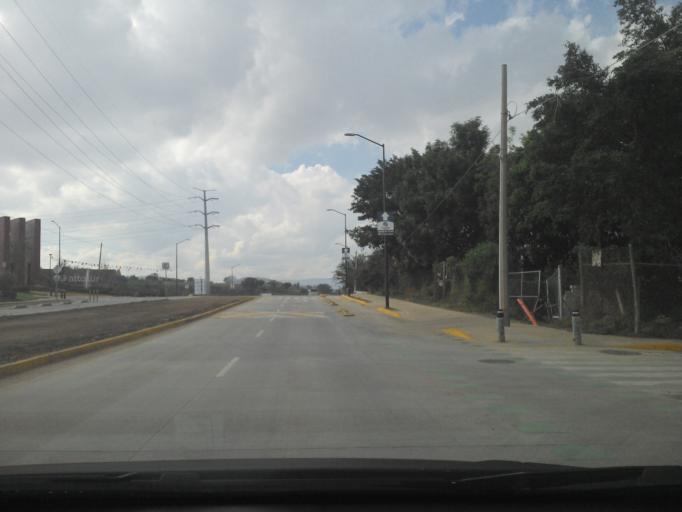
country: MX
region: Jalisco
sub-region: Tlajomulco de Zuniga
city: Altus Bosques
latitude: 20.6148
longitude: -103.3619
